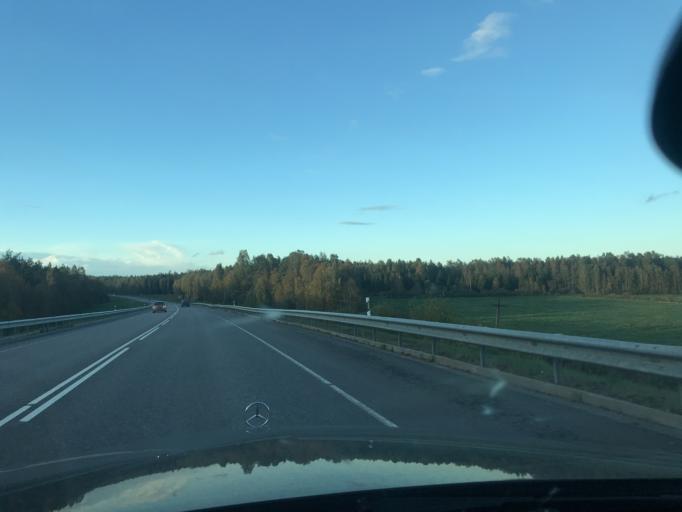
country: EE
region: Vorumaa
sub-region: Voru linn
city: Voru
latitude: 57.8278
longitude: 27.0633
